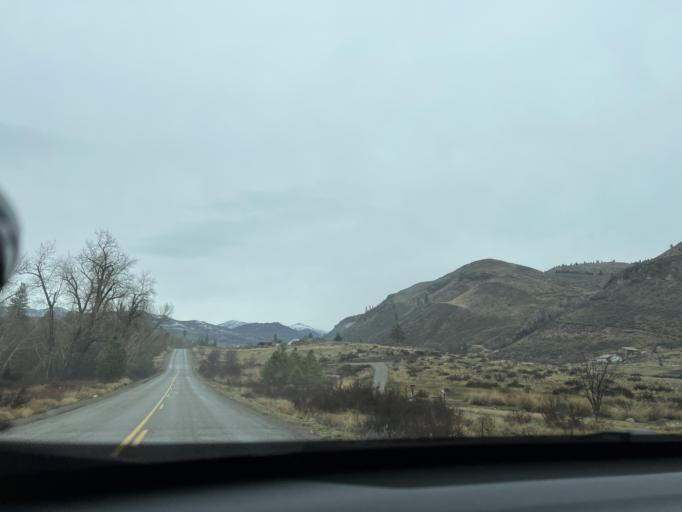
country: US
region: Washington
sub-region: Okanogan County
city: Brewster
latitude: 48.5216
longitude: -120.1780
